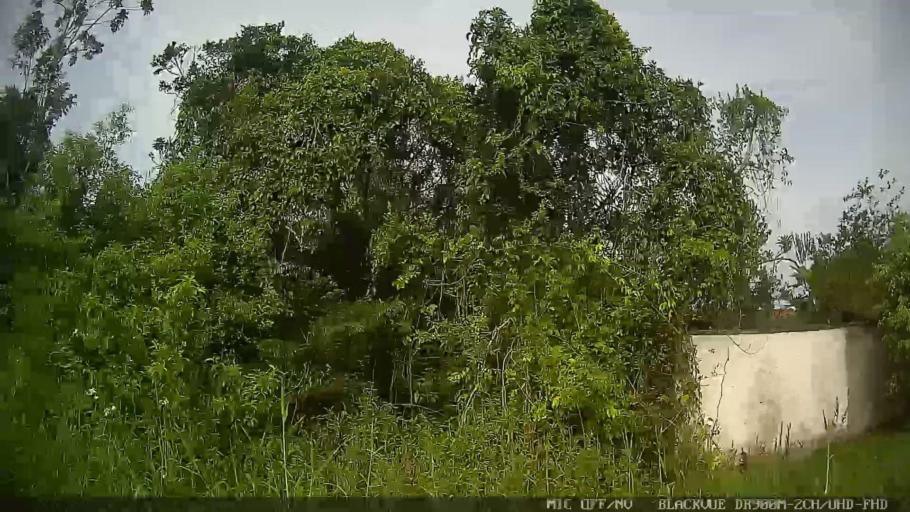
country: BR
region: Sao Paulo
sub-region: Peruibe
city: Peruibe
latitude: -24.2310
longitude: -46.9158
